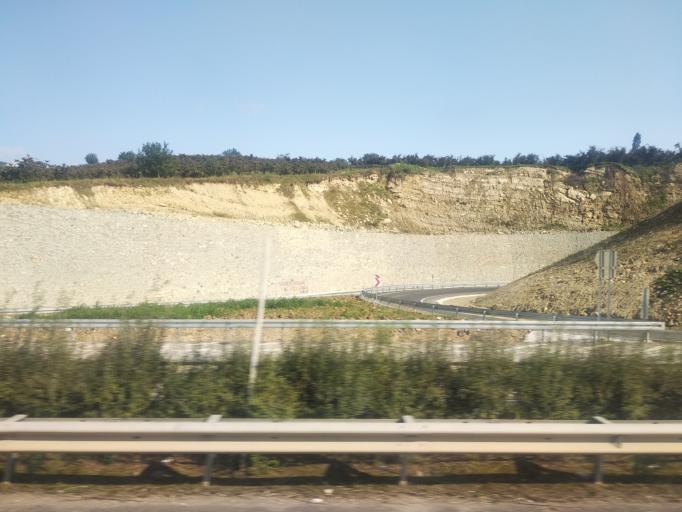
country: TR
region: Ordu
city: Ordu
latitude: 40.9938
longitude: 37.8169
